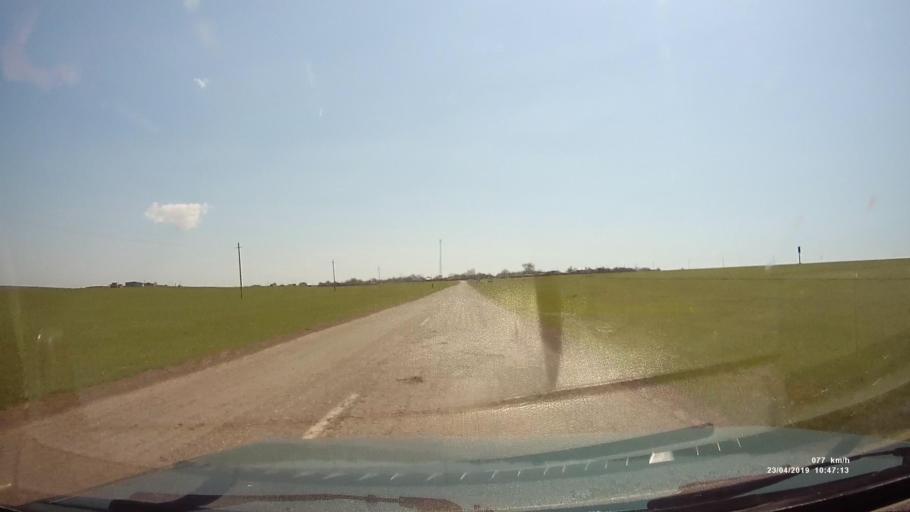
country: RU
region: Kalmykiya
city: Yashalta
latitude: 46.4368
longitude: 42.7034
